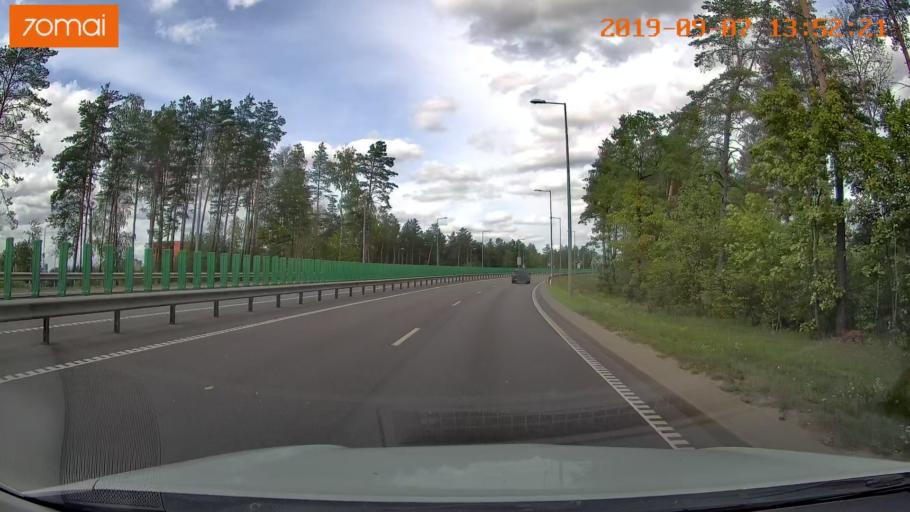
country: LT
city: Baltoji Voke
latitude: 54.6264
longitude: 25.1517
